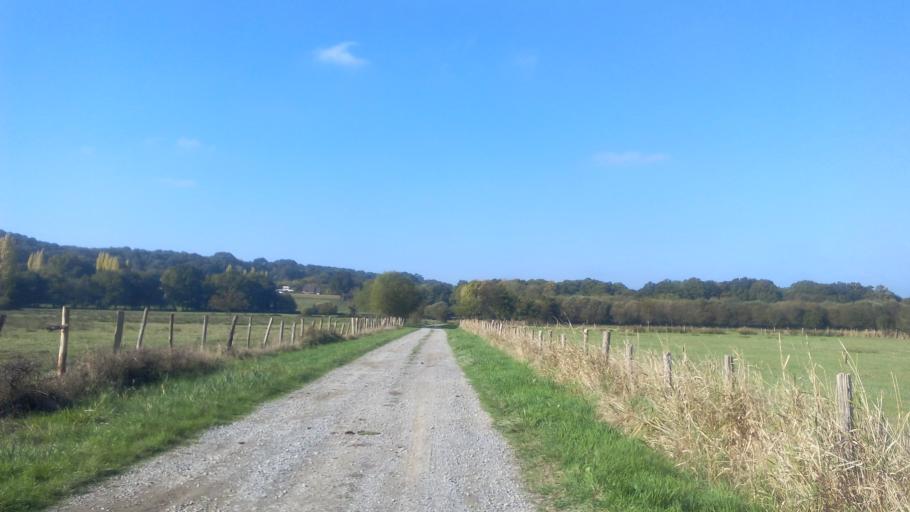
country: FR
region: Brittany
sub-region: Departement du Morbihan
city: Saint-Jean-la-Poterie
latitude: 47.6507
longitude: -2.1149
